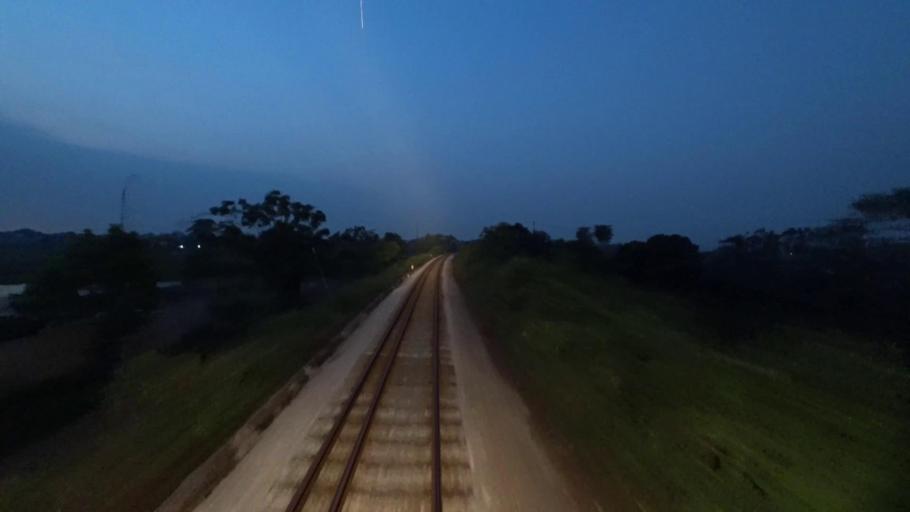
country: VN
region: Ha Noi
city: Soc Son
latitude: 21.2751
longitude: 105.8625
